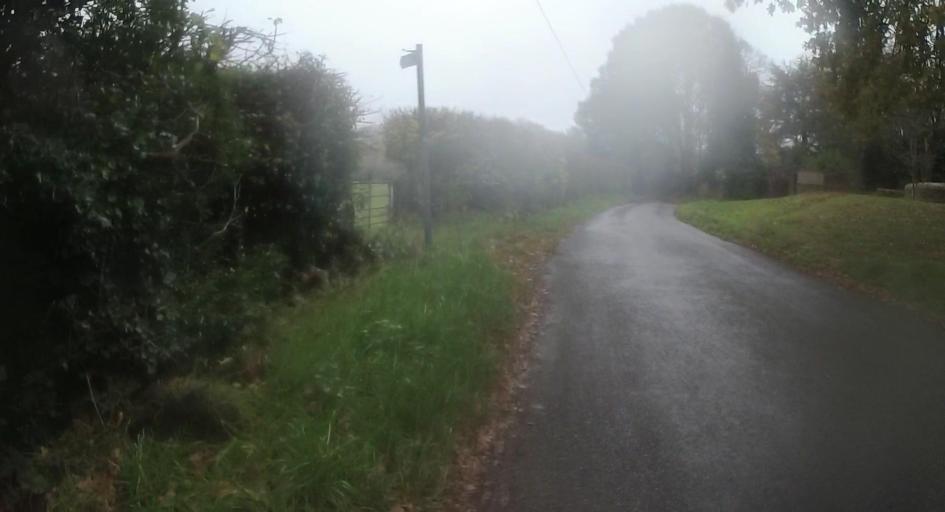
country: GB
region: England
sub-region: Wokingham
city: Finchampstead
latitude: 51.3681
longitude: -0.8611
